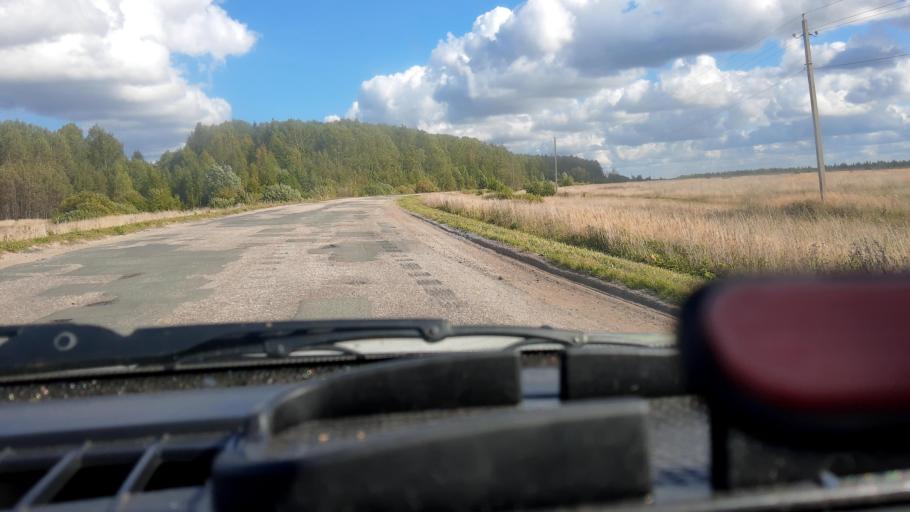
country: RU
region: Mariy-El
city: Kilemary
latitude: 56.9408
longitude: 46.6590
